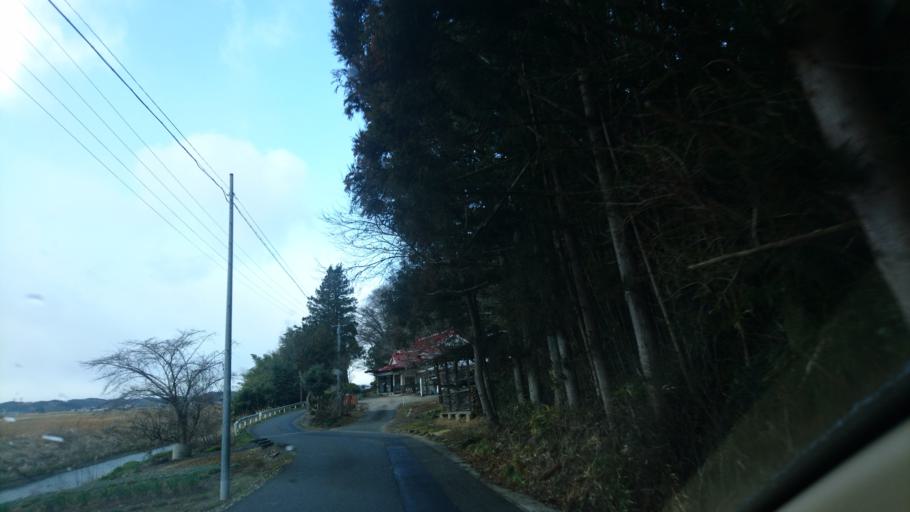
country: JP
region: Iwate
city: Ichinoseki
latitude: 38.7868
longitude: 141.0376
